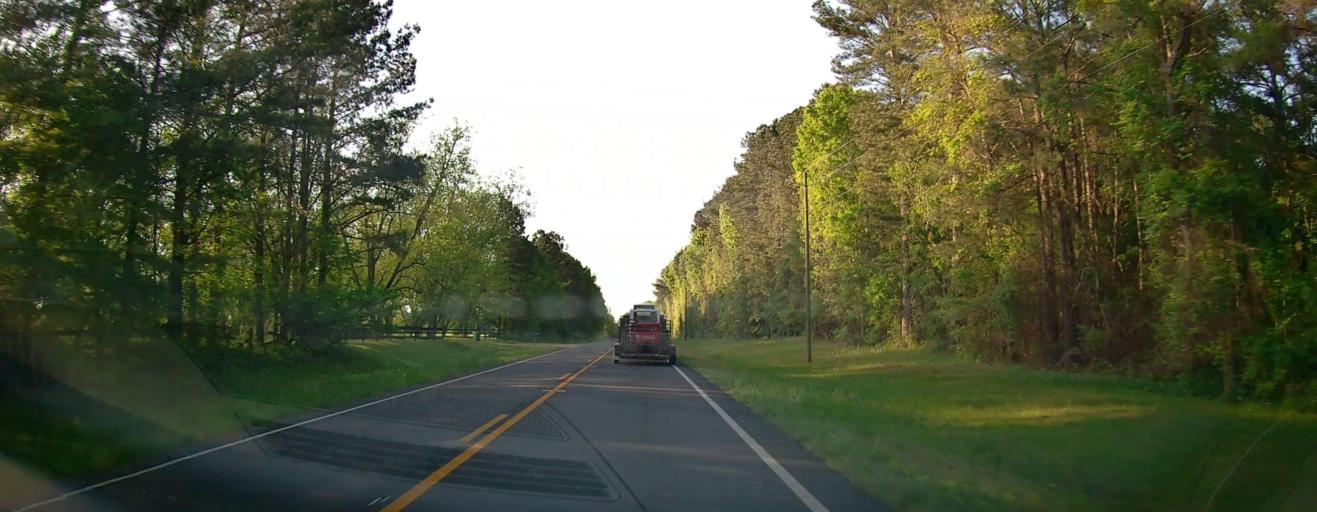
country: US
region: Georgia
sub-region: Jasper County
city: Monticello
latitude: 33.4561
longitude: -83.6313
